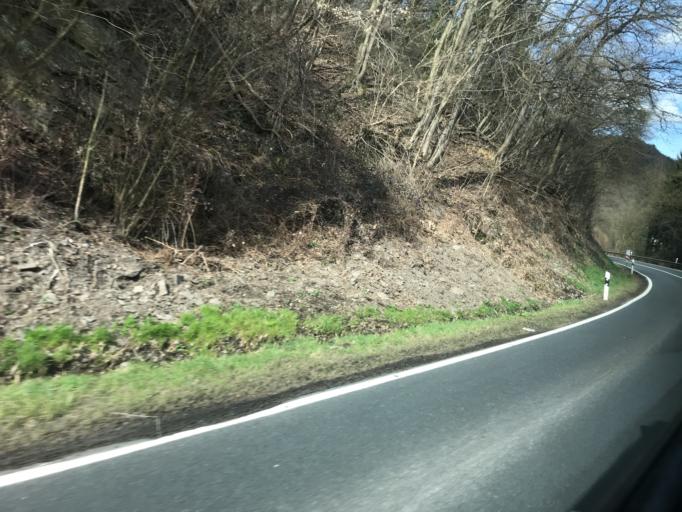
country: DE
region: Rheinland-Pfalz
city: Brohl-Lutzing
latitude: 50.4740
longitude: 7.3144
